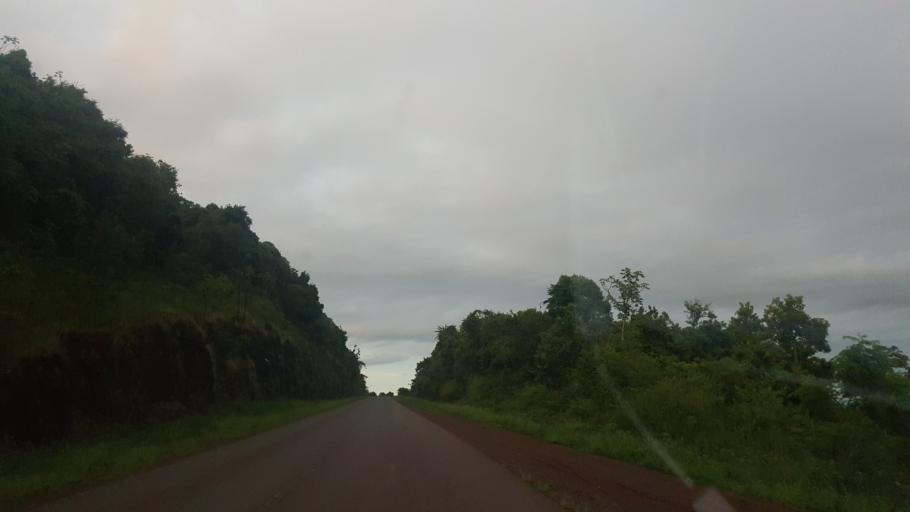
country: AR
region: Misiones
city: Dos de Mayo
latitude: -26.9061
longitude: -54.7363
